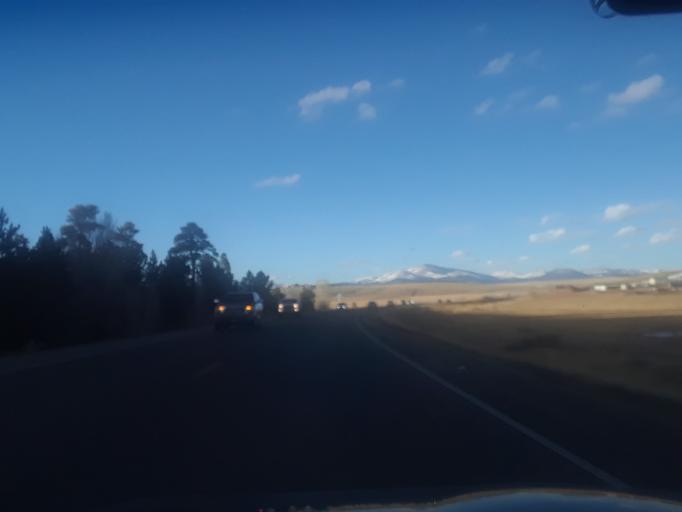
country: US
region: Colorado
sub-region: Park County
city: Fairplay
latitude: 39.0473
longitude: -105.9750
